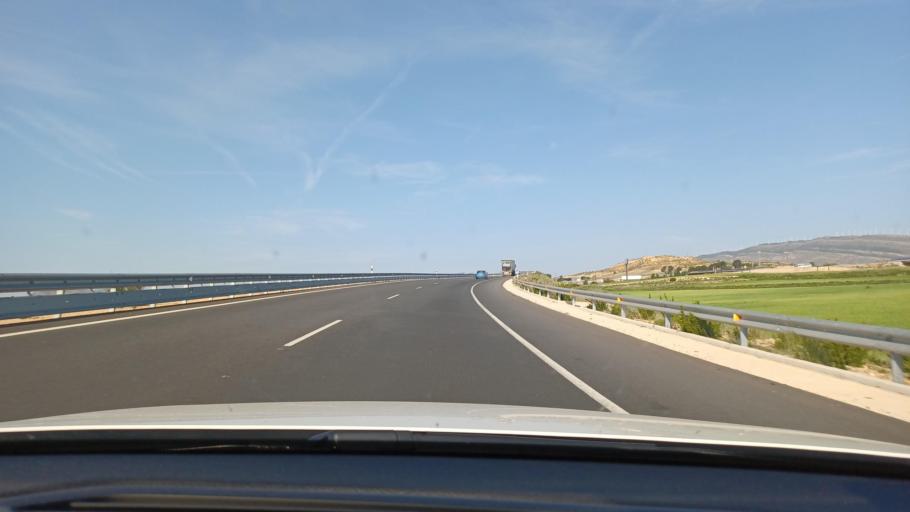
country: ES
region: Castille-La Mancha
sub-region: Provincia de Albacete
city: Caudete
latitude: 38.7313
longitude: -0.9304
